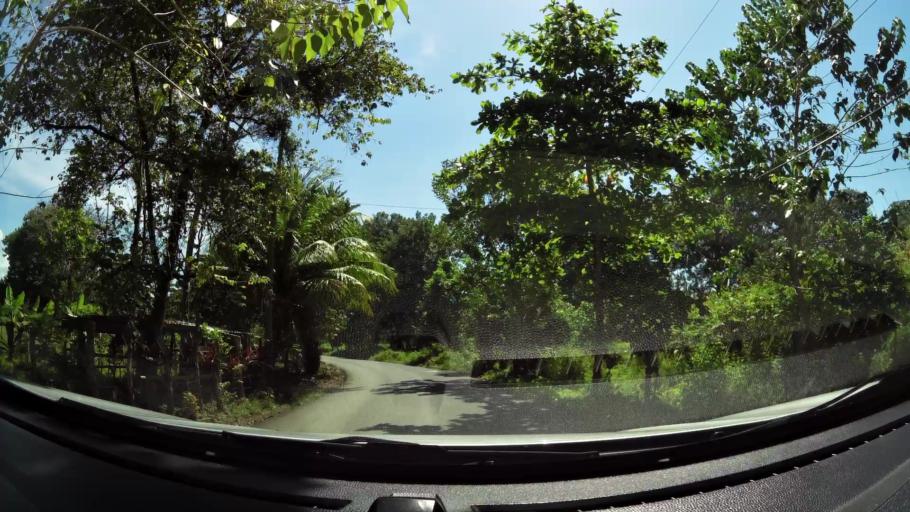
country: CR
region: Puntarenas
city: Quepos
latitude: 9.3223
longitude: -83.9586
